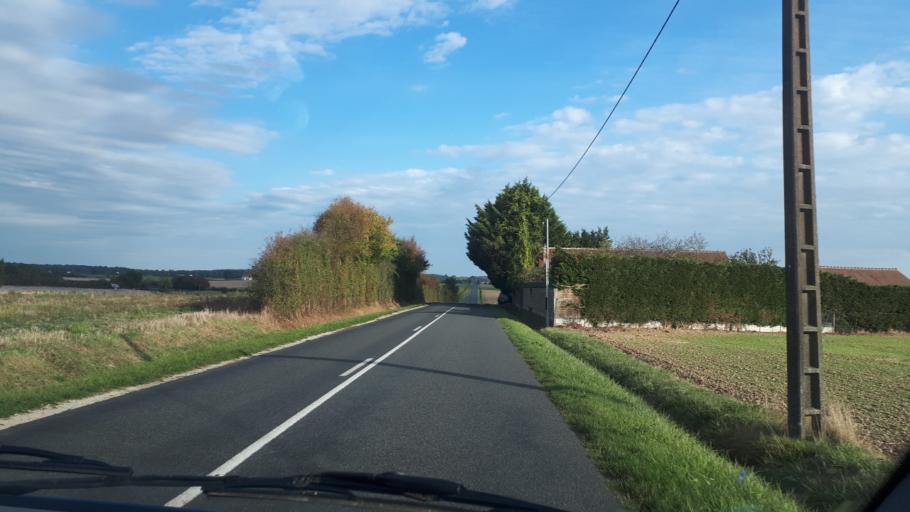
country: FR
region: Centre
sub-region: Departement du Loir-et-Cher
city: Sarge-sur-Braye
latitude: 47.9063
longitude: 0.9304
